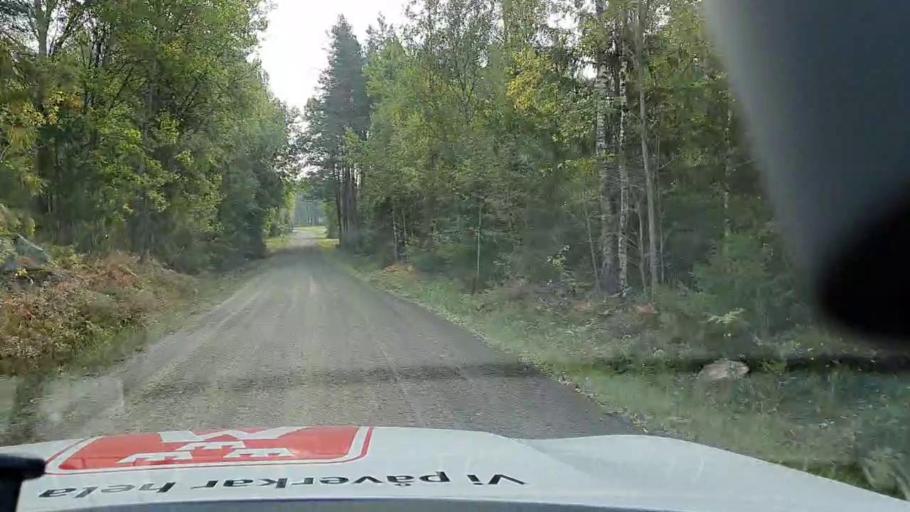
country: SE
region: Vaestmanland
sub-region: Kungsors Kommun
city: Kungsoer
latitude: 59.3620
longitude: 16.1408
